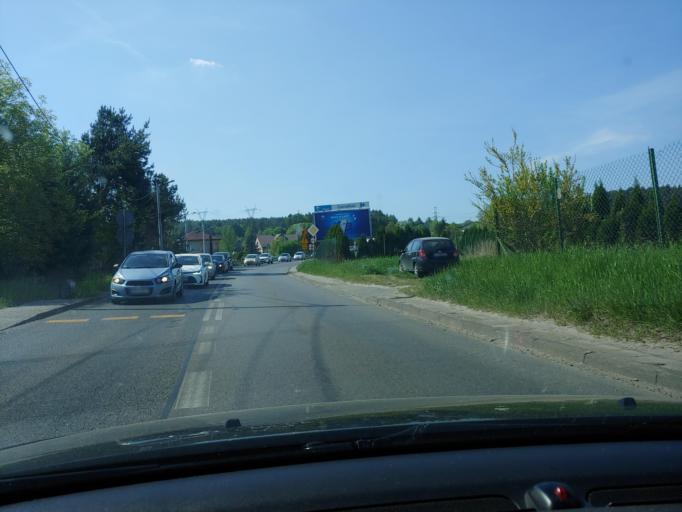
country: PL
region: Silesian Voivodeship
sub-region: Jaworzno
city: Jaworzno
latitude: 50.1648
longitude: 19.3043
